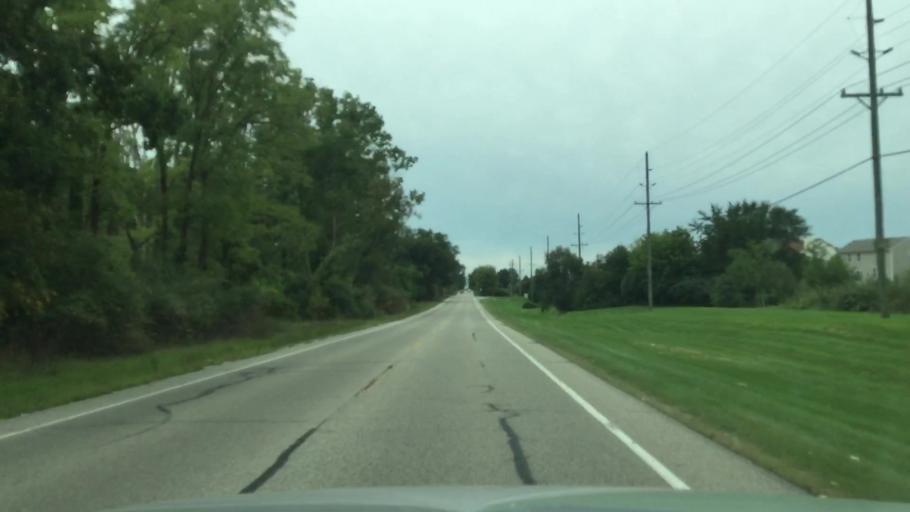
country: US
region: Michigan
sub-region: Washtenaw County
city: Ypsilanti
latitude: 42.2139
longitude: -83.6601
